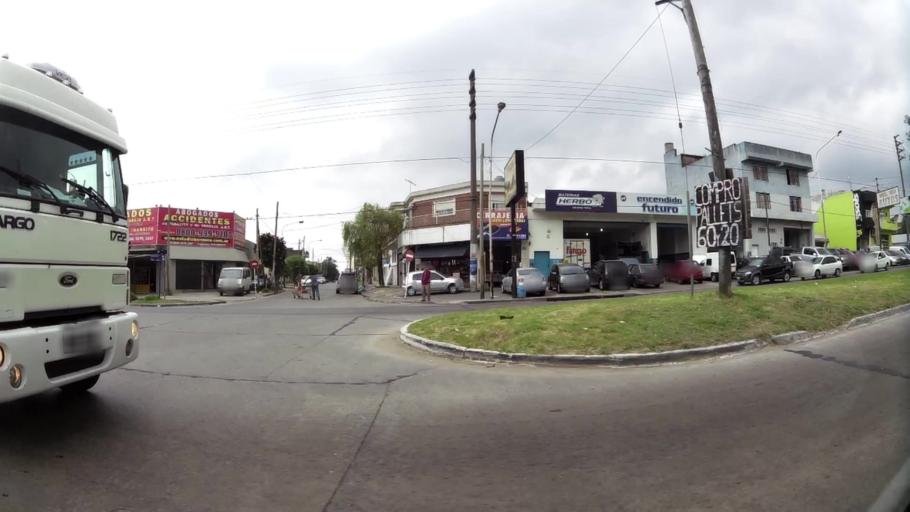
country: AR
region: Buenos Aires
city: San Justo
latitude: -34.6983
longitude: -58.5385
